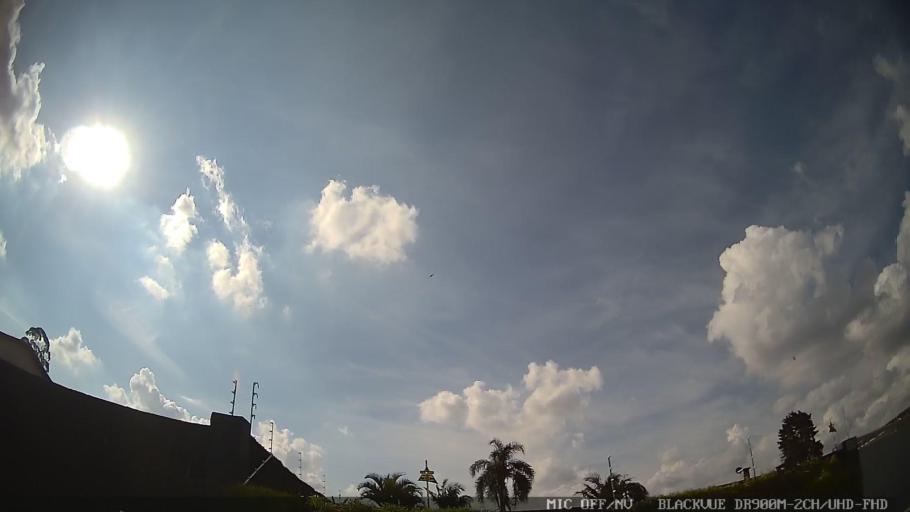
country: BR
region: Sao Paulo
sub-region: Braganca Paulista
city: Braganca Paulista
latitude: -22.9907
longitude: -46.5289
